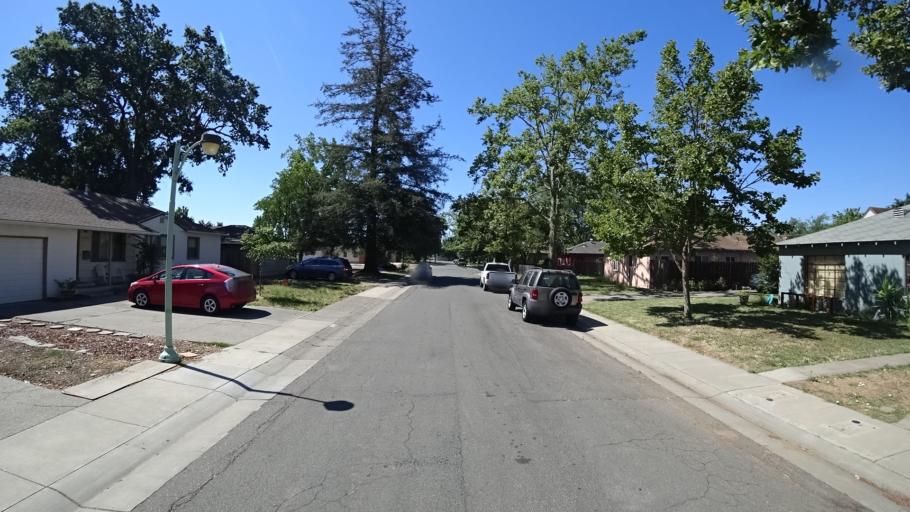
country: US
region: California
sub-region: Sacramento County
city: Parkway
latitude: 38.5262
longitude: -121.4949
